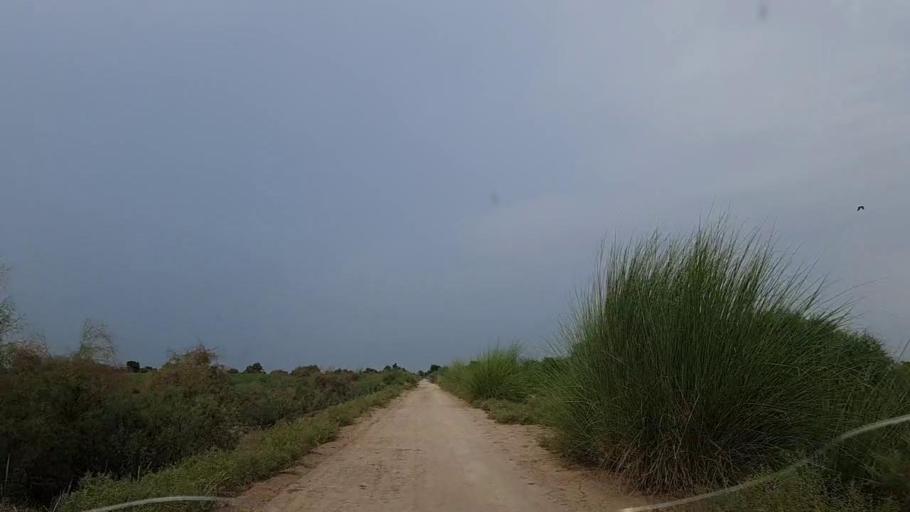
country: PK
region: Sindh
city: Khanpur
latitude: 27.8265
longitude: 69.5590
